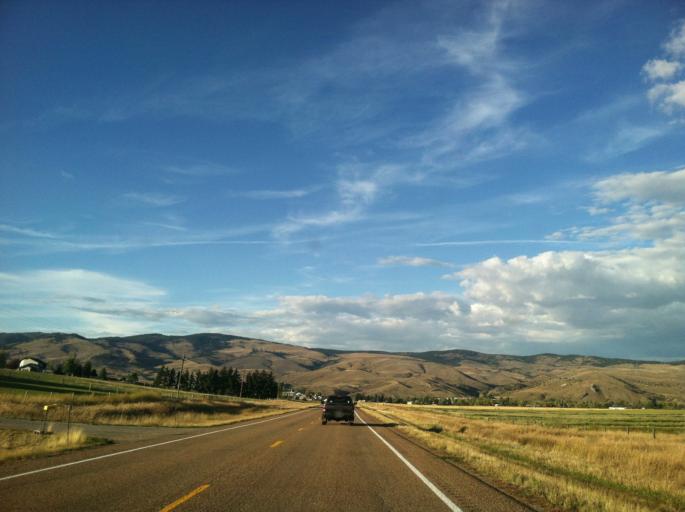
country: US
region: Montana
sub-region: Granite County
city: Philipsburg
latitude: 46.6489
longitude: -113.1626
